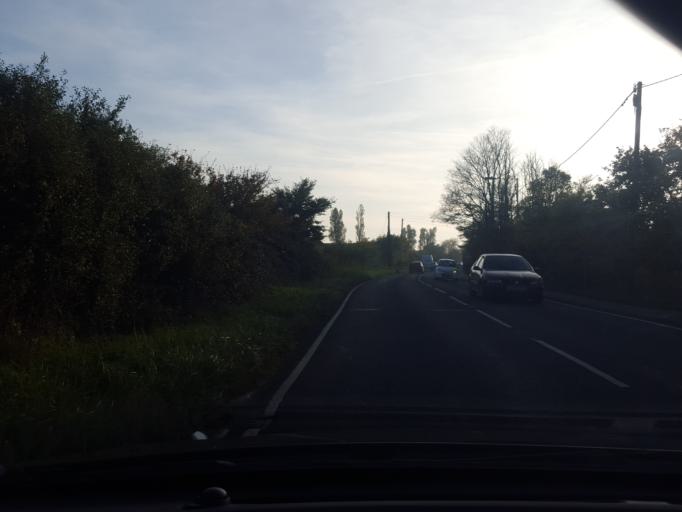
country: GB
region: England
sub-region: Essex
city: Frinton-on-Sea
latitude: 51.8381
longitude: 1.2155
